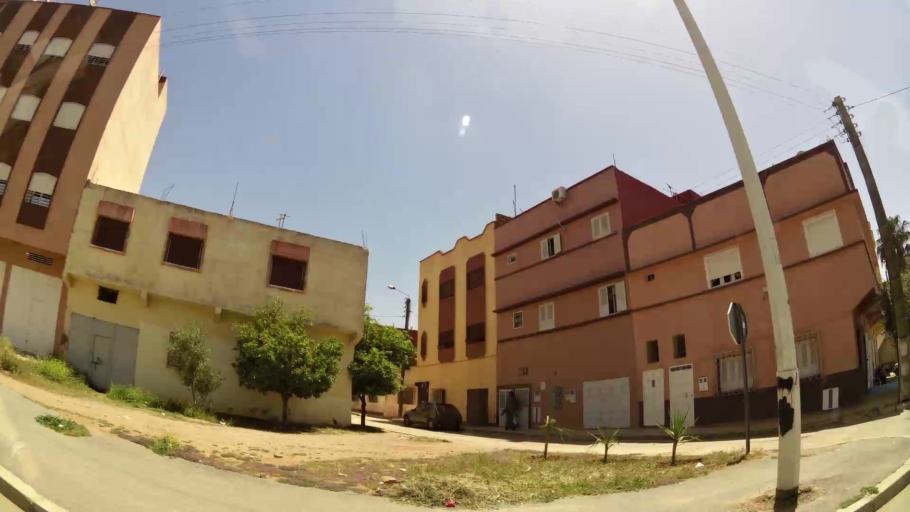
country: MA
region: Rabat-Sale-Zemmour-Zaer
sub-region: Khemisset
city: Khemisset
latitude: 33.8309
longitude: -6.0778
